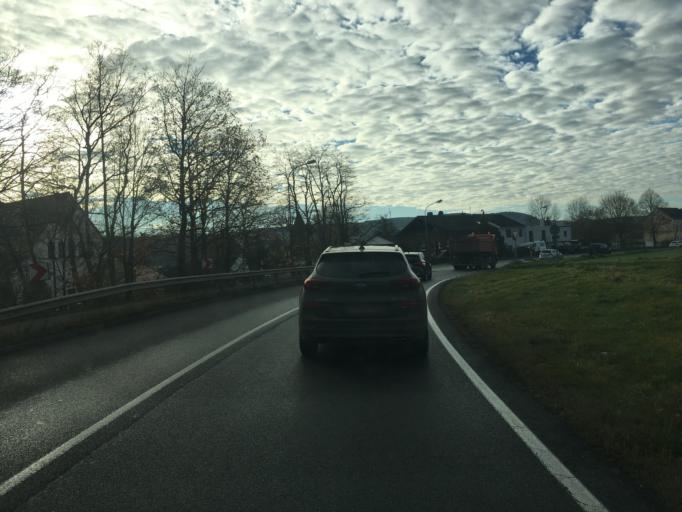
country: DE
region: North Rhine-Westphalia
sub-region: Regierungsbezirk Koln
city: Mechernich
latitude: 50.5933
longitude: 6.6304
